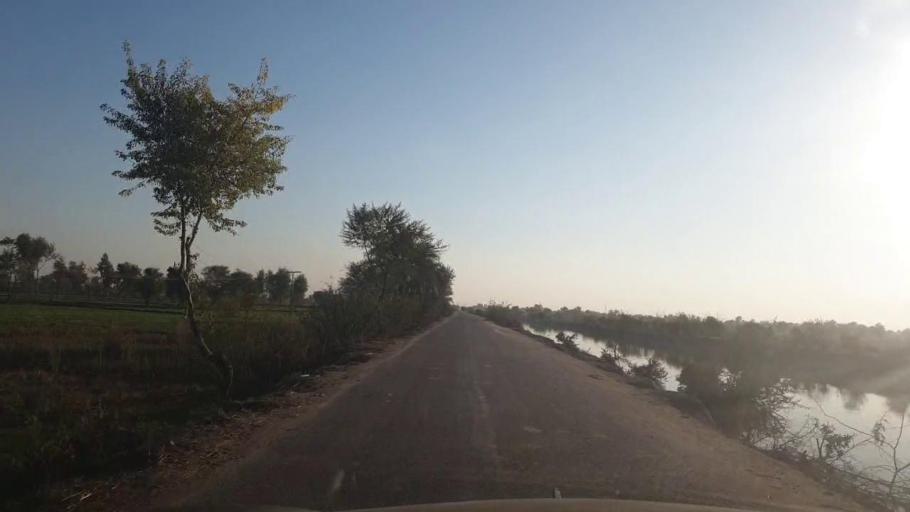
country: PK
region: Sindh
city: Mirpur Mathelo
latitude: 28.0055
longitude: 69.4697
